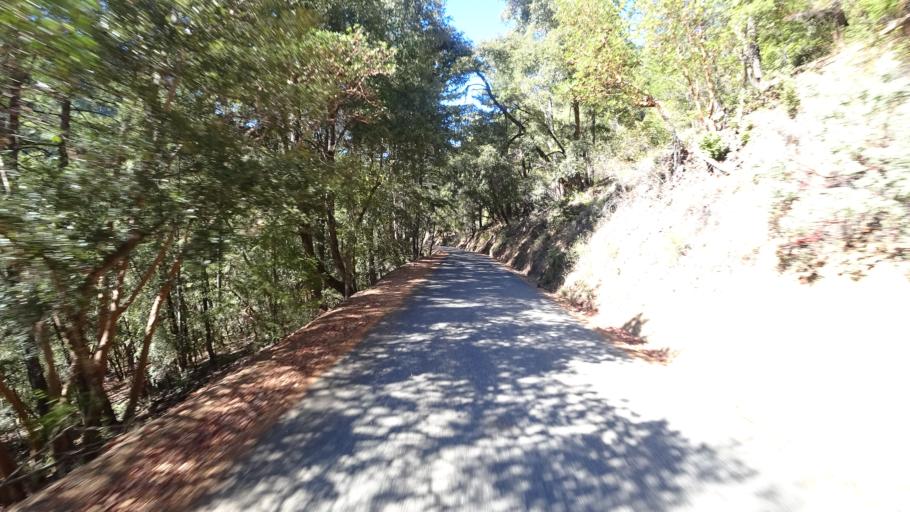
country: US
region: California
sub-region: Humboldt County
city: Willow Creek
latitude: 41.2839
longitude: -123.3544
